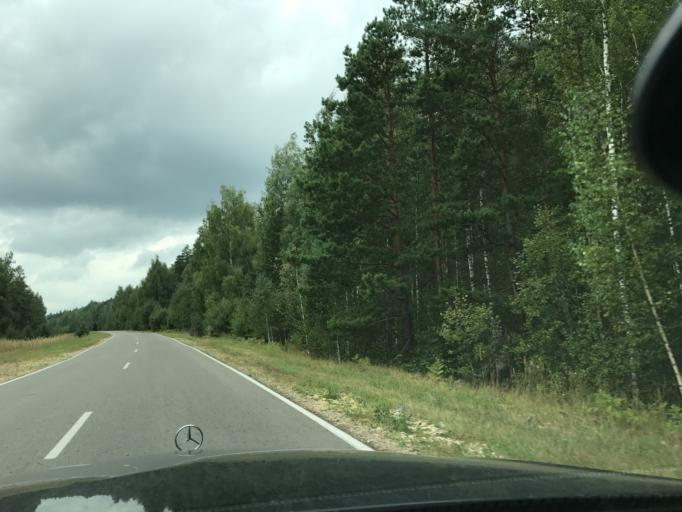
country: RU
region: Nizjnij Novgorod
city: Taremskoye
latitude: 56.0144
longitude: 42.9417
